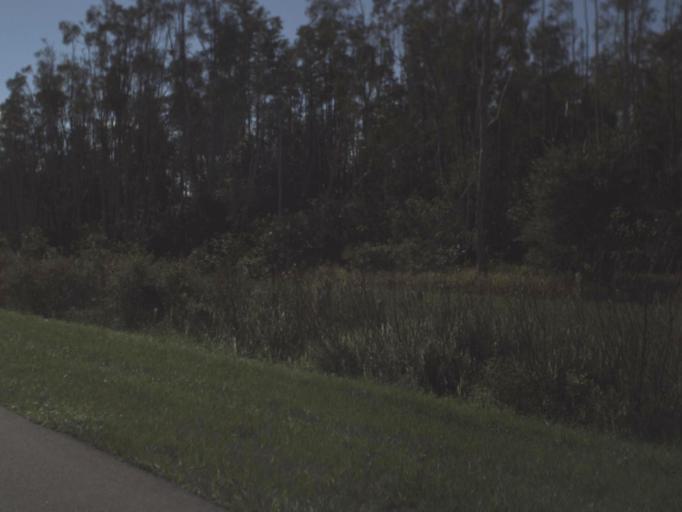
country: US
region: Florida
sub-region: Lee County
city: Lehigh Acres
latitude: 26.5501
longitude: -81.6436
